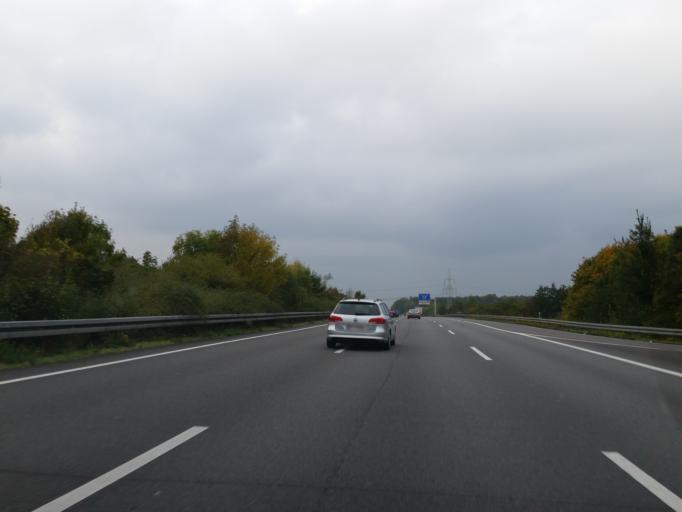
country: DE
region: Lower Saxony
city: Lehrte
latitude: 52.3828
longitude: 10.0198
